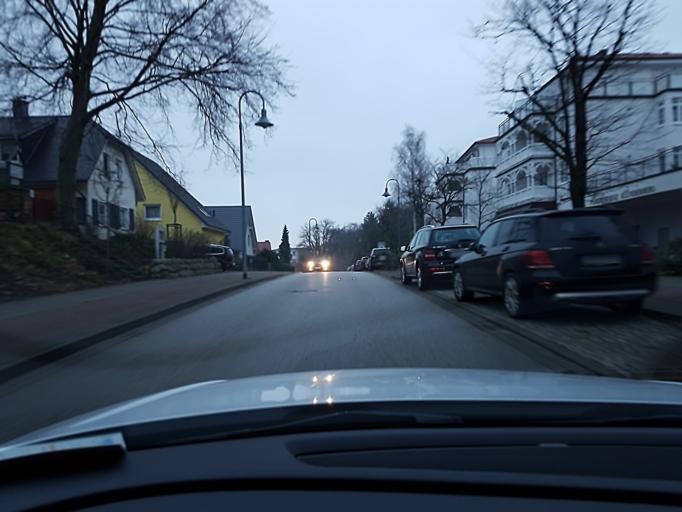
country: DE
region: Mecklenburg-Vorpommern
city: Ostseebad Binz
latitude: 54.3946
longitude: 13.6140
